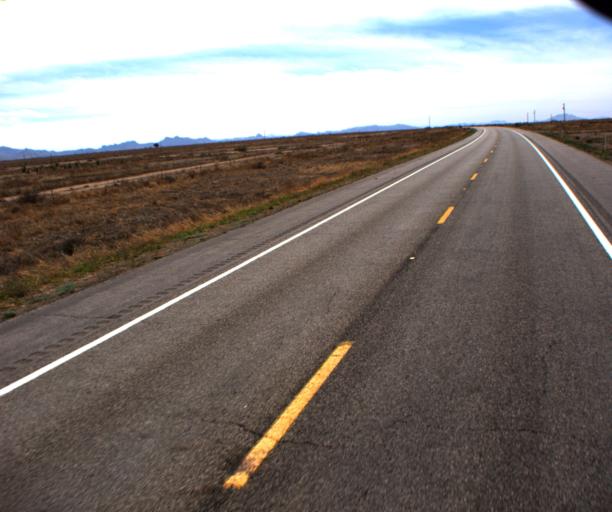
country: US
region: Arizona
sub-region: Cochise County
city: Pirtleville
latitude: 31.5585
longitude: -109.6662
